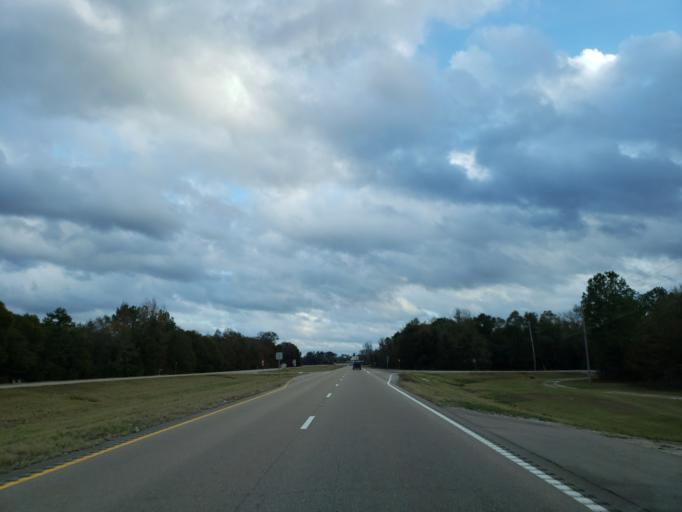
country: US
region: Mississippi
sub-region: Perry County
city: New Augusta
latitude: 31.1331
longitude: -88.8558
